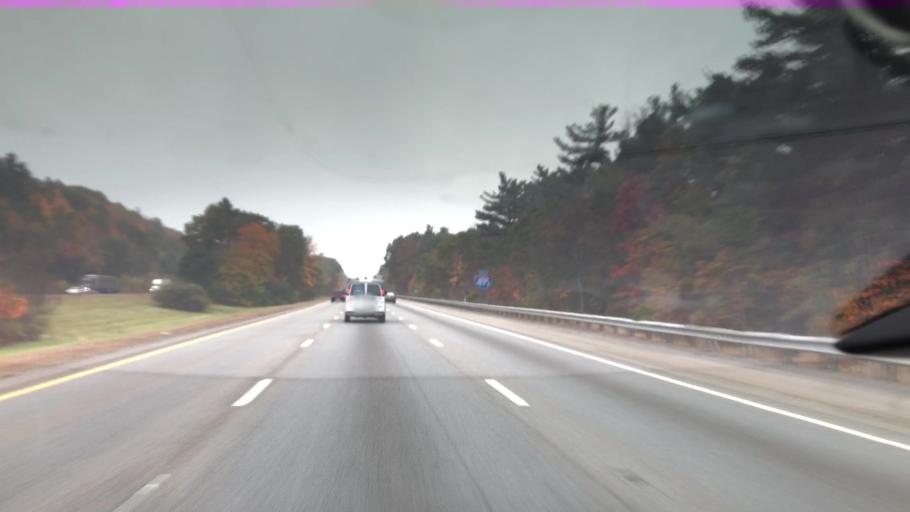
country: US
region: Massachusetts
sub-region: Worcester County
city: Harvard
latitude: 42.4660
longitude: -71.5639
